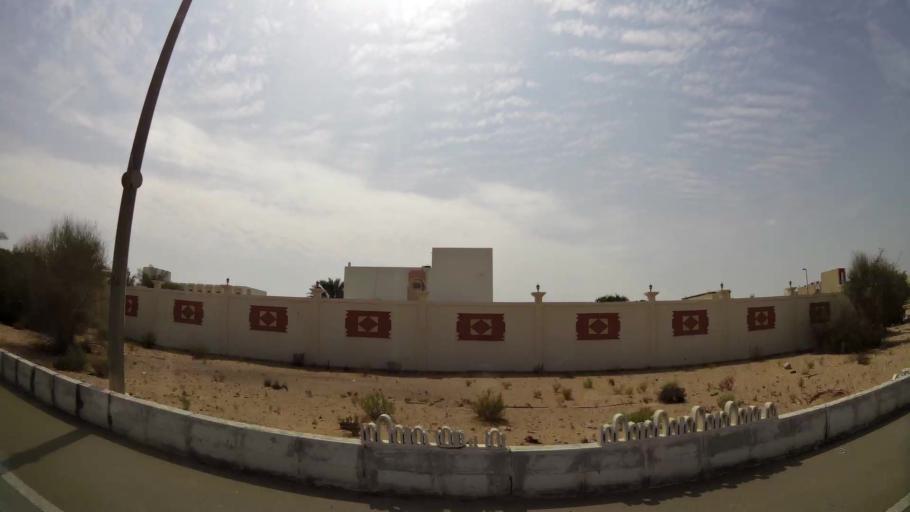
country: AE
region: Abu Dhabi
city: Abu Dhabi
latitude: 24.5477
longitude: 54.6687
